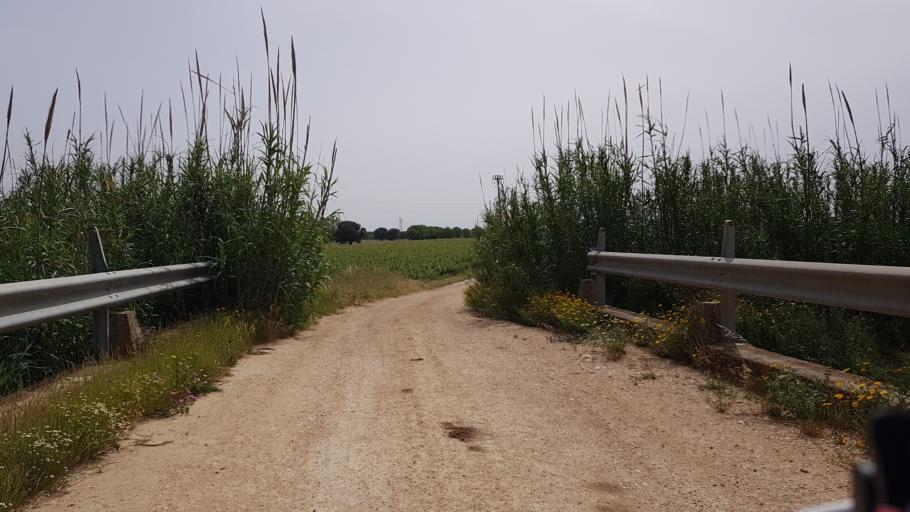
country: IT
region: Apulia
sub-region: Provincia di Brindisi
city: Mesagne
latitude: 40.6324
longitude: 17.8143
